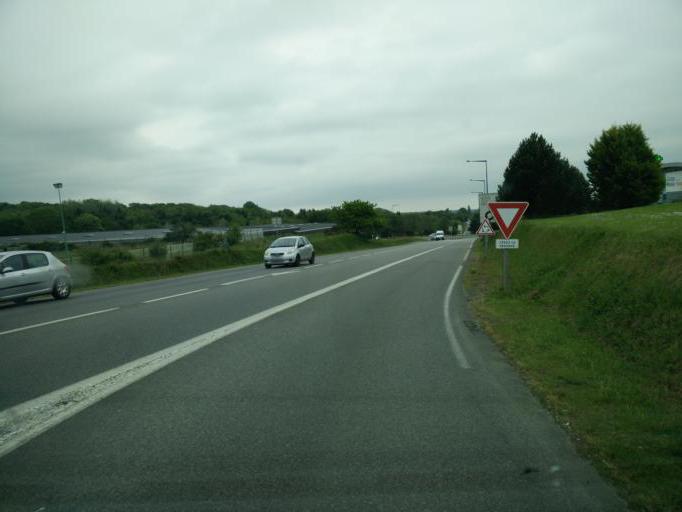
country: FR
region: Brittany
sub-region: Departement du Finistere
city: Concarneau
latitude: 47.8876
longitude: -3.9146
